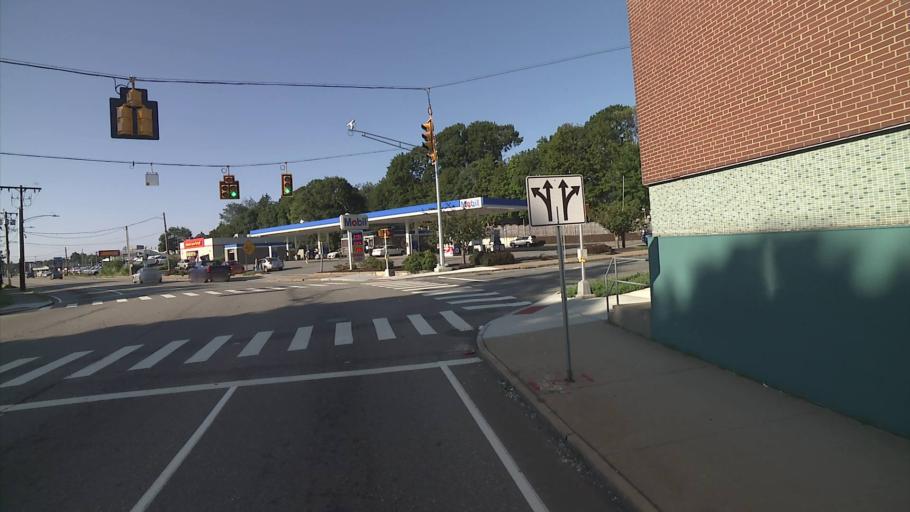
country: US
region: Connecticut
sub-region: New London County
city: New London
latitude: 41.3675
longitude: -72.1168
